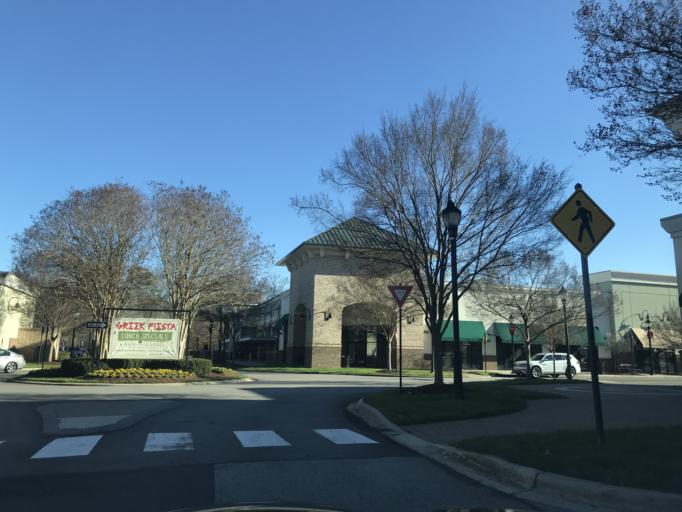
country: US
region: North Carolina
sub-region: Wake County
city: Morrisville
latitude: 35.9001
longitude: -78.7930
